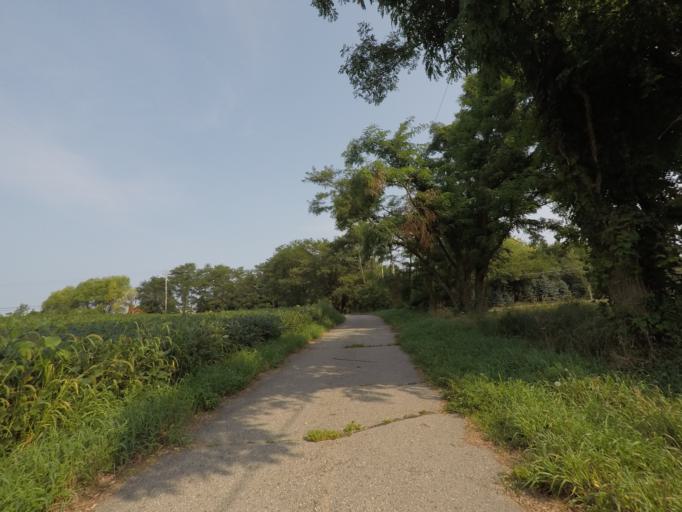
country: US
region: Wisconsin
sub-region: Waukesha County
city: Dousman
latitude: 43.0209
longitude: -88.4476
